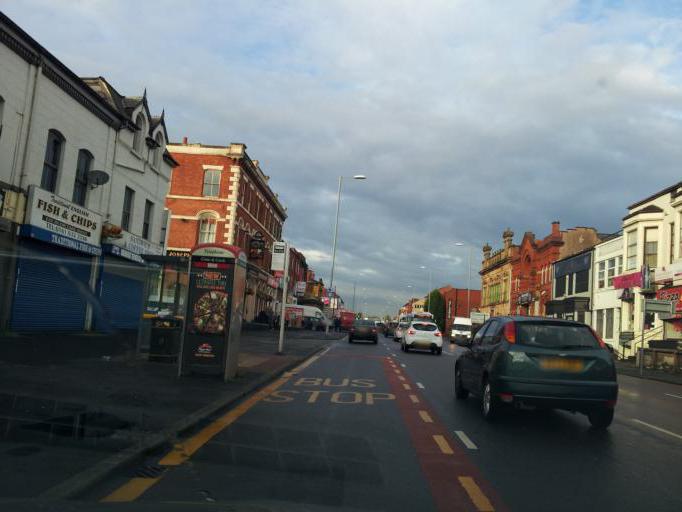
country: GB
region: England
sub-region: Manchester
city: Cheetham Hill
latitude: 53.4925
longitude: -2.2402
